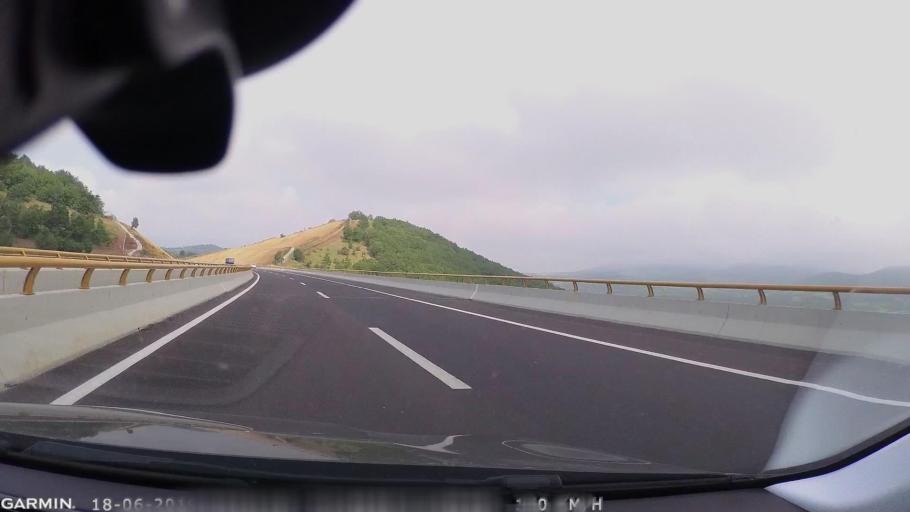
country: MK
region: Sveti Nikole
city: Gorobinci
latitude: 41.9212
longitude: 21.8649
